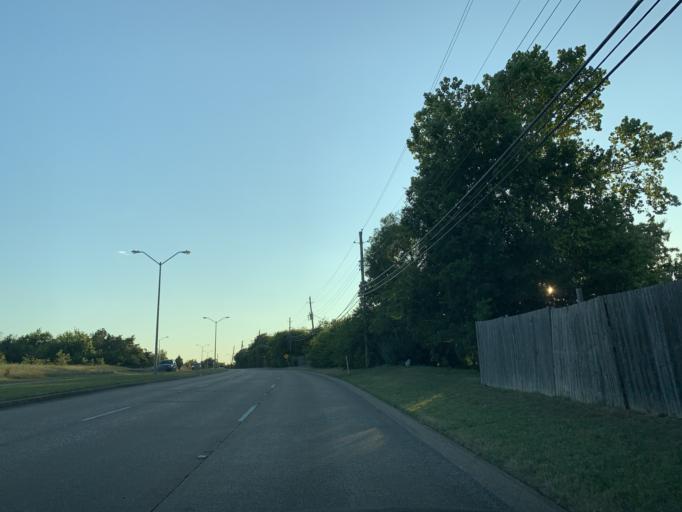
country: US
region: Texas
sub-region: Dallas County
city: Lancaster
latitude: 32.6634
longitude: -96.8003
